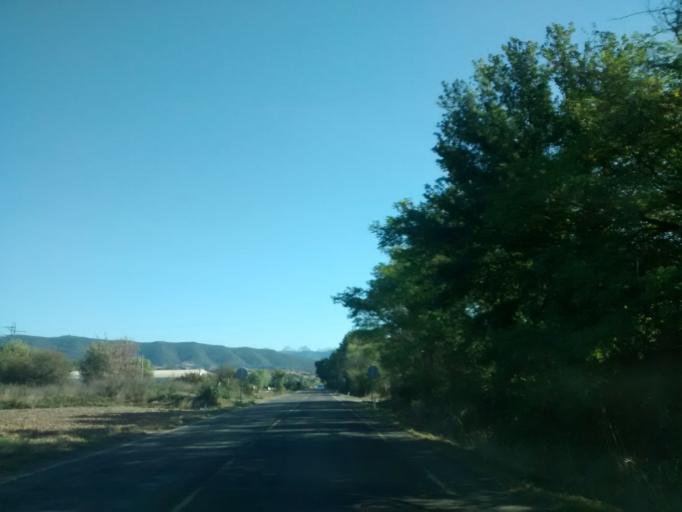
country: ES
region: Aragon
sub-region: Provincia de Huesca
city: Bailo
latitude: 42.5647
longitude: -0.7776
